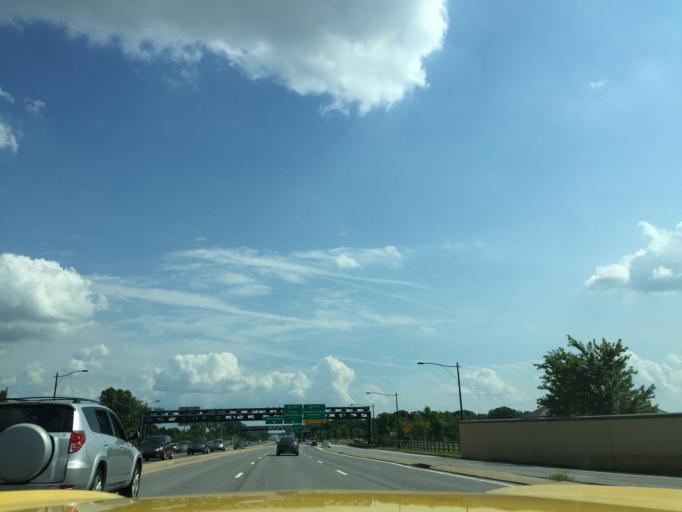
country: US
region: Delaware
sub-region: New Castle County
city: Wilmington
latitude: 39.7771
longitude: -75.5446
